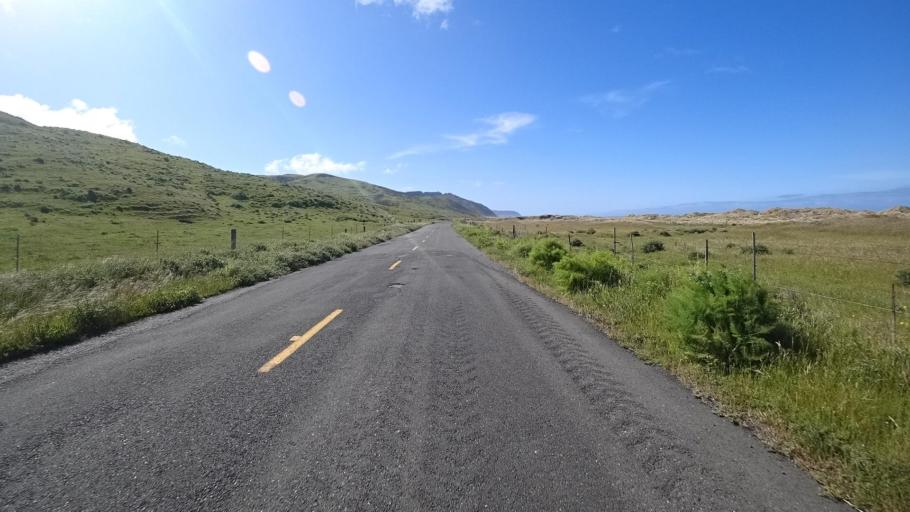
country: US
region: California
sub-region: Humboldt County
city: Ferndale
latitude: 40.3721
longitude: -124.3630
